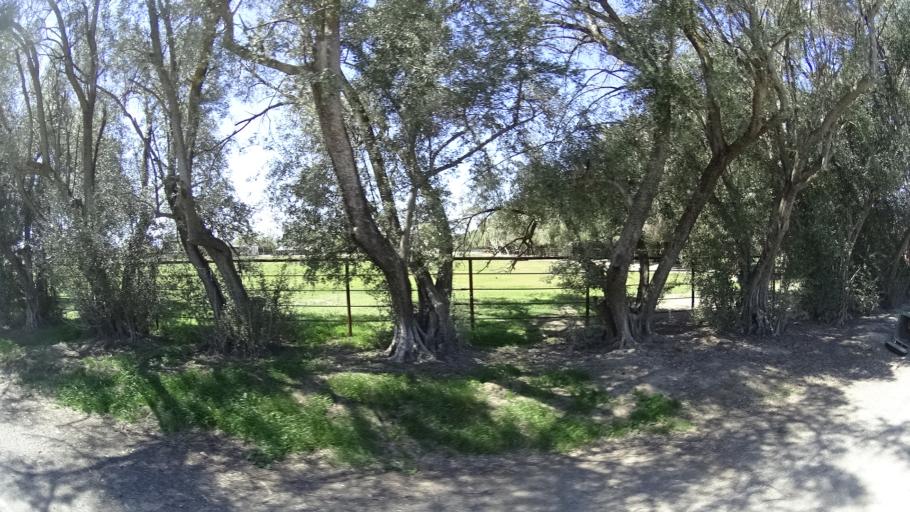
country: US
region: California
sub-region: Glenn County
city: Orland
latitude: 39.7731
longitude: -122.2387
